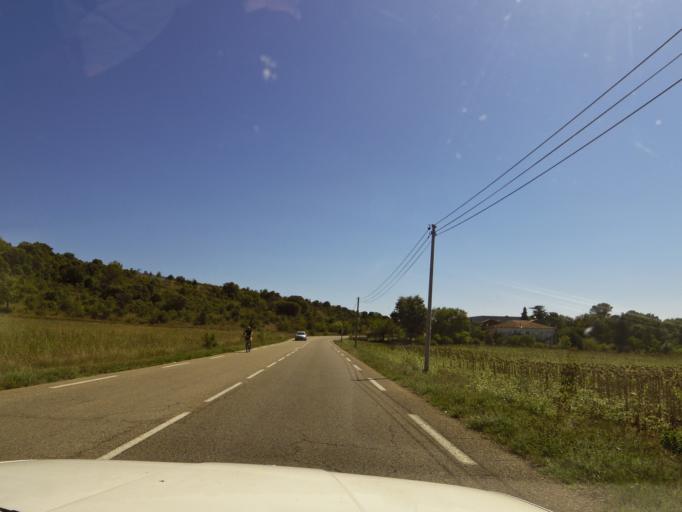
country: FR
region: Languedoc-Roussillon
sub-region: Departement du Gard
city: Saint-Hilaire-de-Brethmas
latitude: 44.0719
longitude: 4.1173
